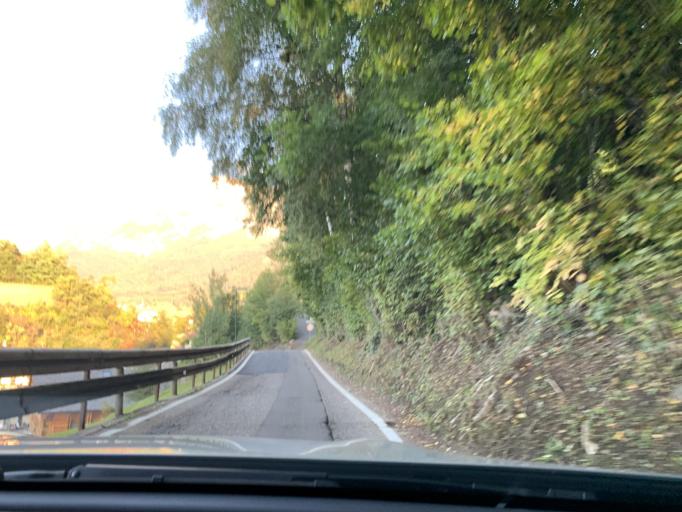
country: IT
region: Trentino-Alto Adige
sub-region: Bolzano
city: Fie Allo Sciliar
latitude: 46.5031
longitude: 11.4953
